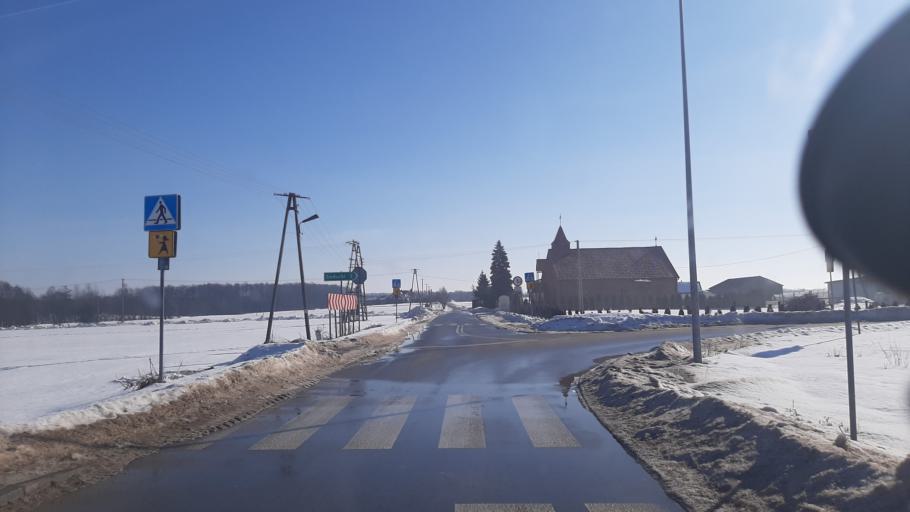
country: PL
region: Lublin Voivodeship
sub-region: Powiat lubelski
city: Garbow
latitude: 51.3047
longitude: 22.3079
